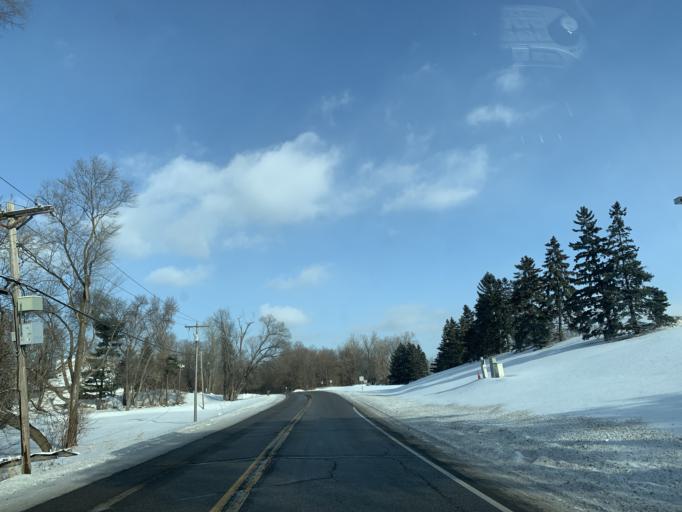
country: US
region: Minnesota
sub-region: Dakota County
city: Inver Grove Heights
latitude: 44.8701
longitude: -93.0654
